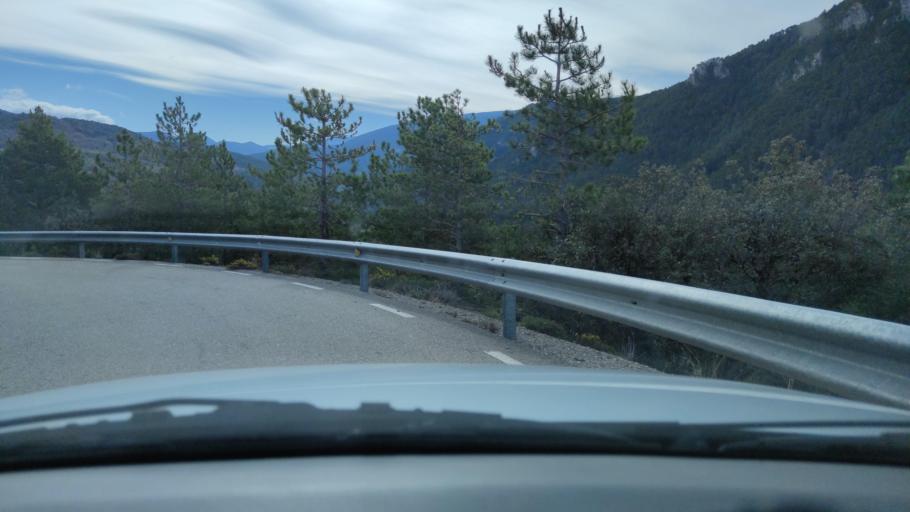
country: ES
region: Catalonia
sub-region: Provincia de Lleida
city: la Seu d'Urgell
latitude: 42.2409
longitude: 1.4284
